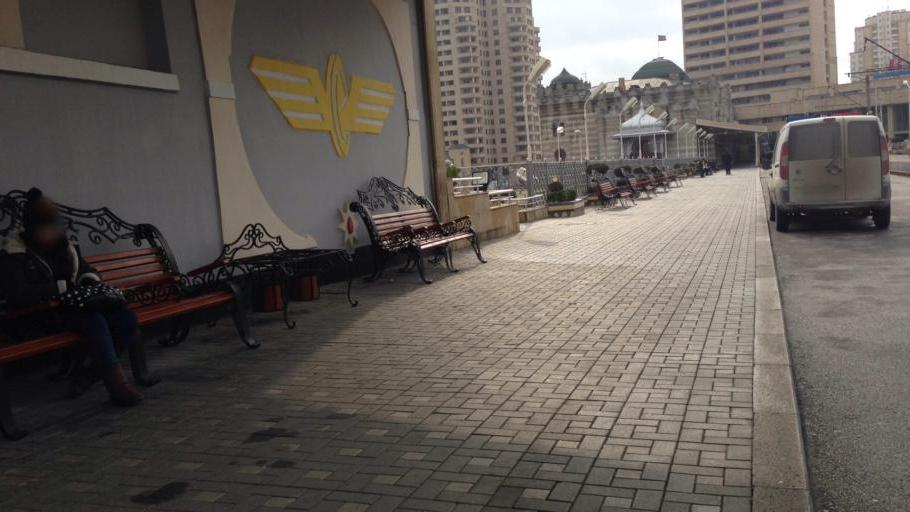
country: AZ
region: Baki
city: Baku
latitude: 40.3814
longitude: 49.8515
